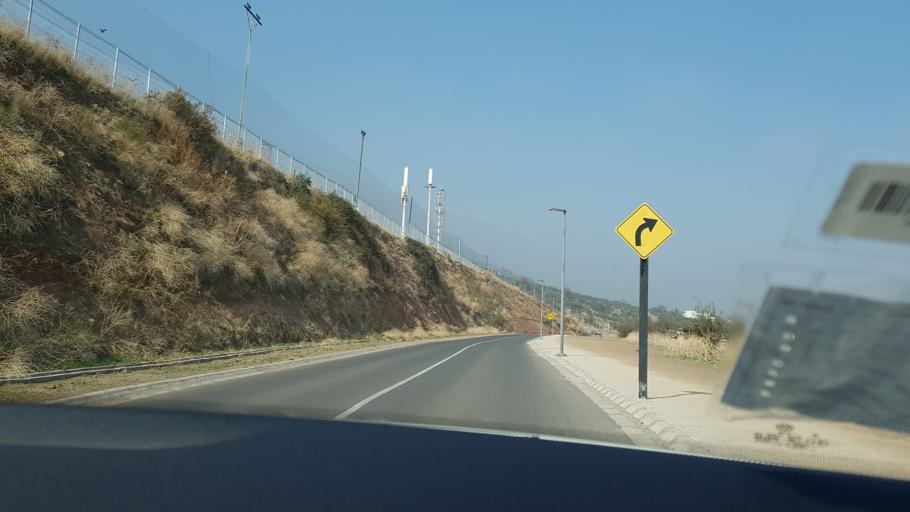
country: CL
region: Santiago Metropolitan
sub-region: Provincia de Santiago
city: Villa Presidente Frei, Nunoa, Santiago, Chile
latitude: -33.4787
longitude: -70.5170
